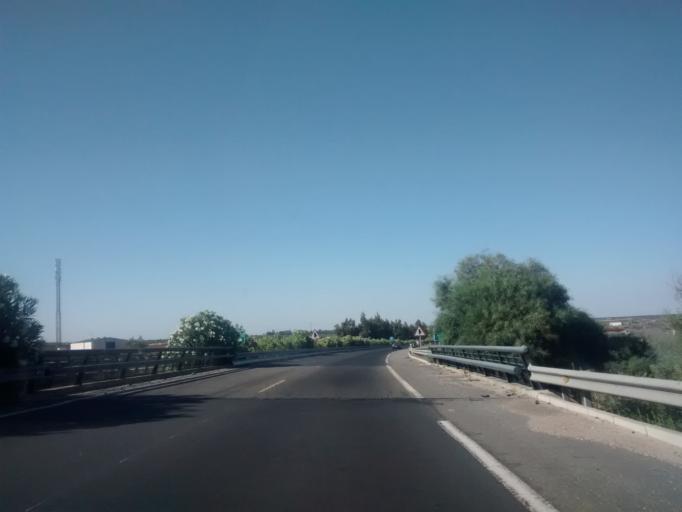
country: ES
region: Andalusia
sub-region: Provincia de Huelva
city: Almonte
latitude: 37.2655
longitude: -6.5311
